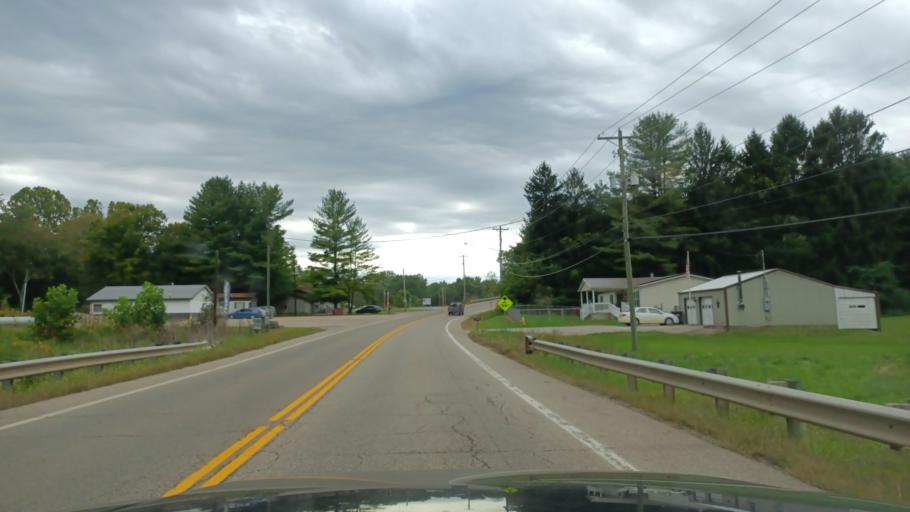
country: US
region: Ohio
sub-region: Vinton County
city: McArthur
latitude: 39.2447
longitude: -82.4684
